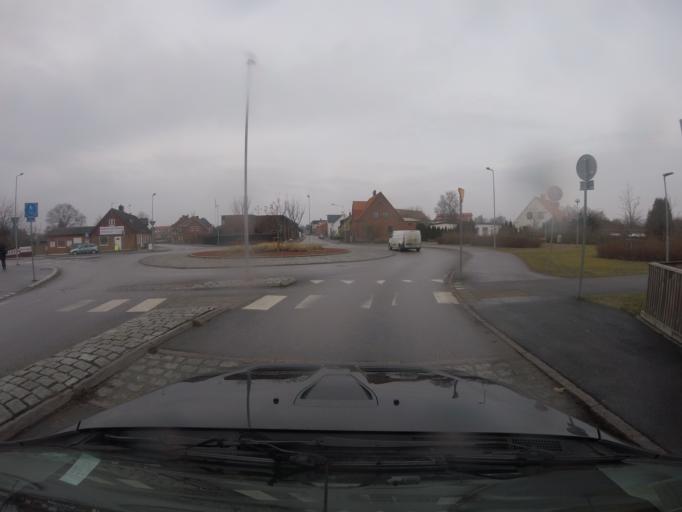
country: SE
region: Skane
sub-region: Svedala Kommun
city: Svedala
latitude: 55.5088
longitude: 13.2428
